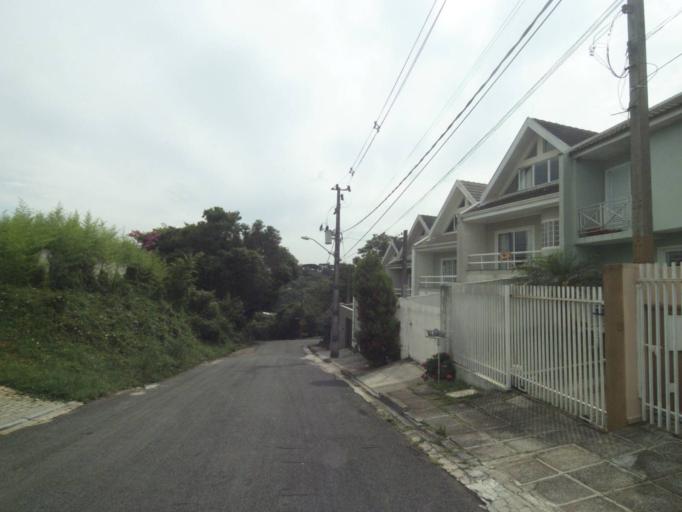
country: BR
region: Parana
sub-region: Curitiba
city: Curitiba
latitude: -25.4047
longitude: -49.2946
